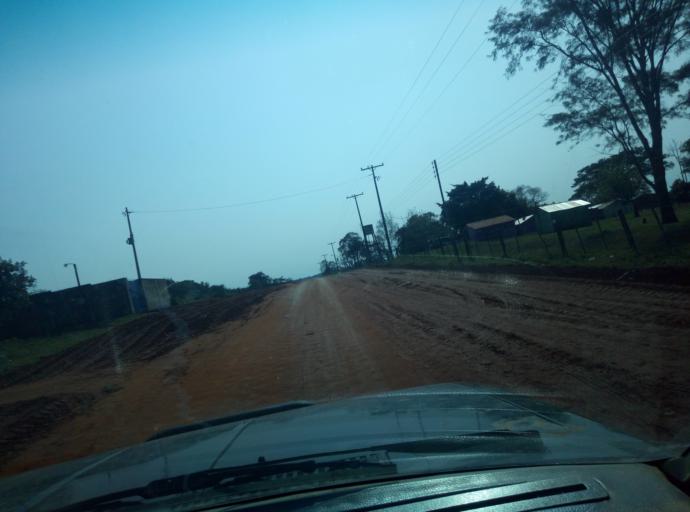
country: PY
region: Caaguazu
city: Carayao
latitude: -25.3152
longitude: -56.3272
